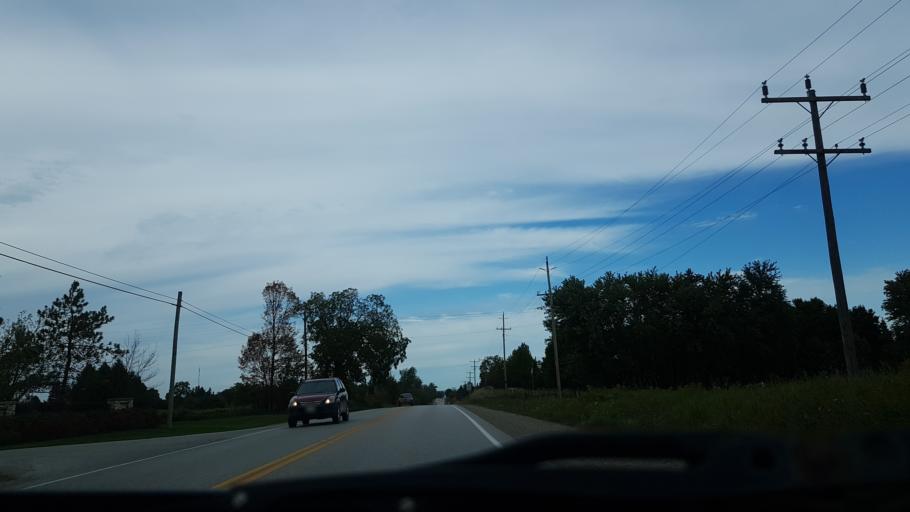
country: CA
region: Ontario
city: Wasaga Beach
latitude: 44.3740
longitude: -80.0863
